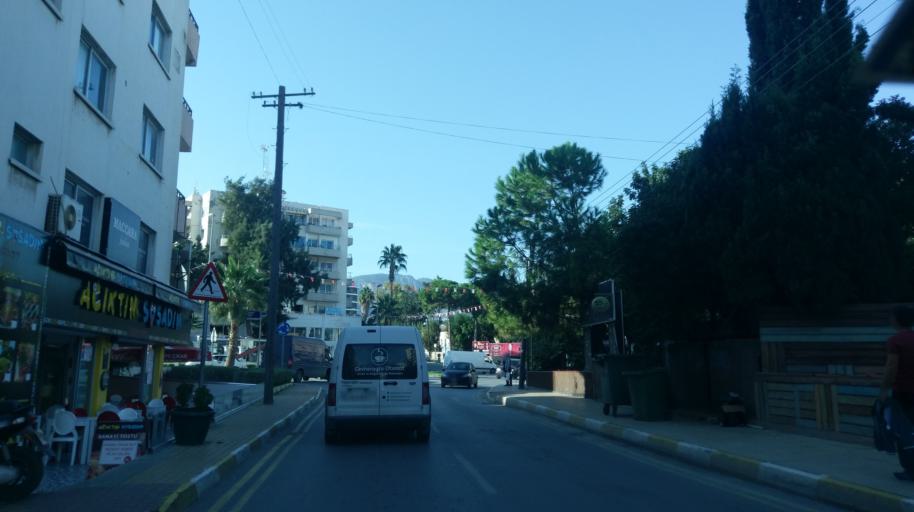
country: CY
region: Keryneia
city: Kyrenia
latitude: 35.3363
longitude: 33.3089
